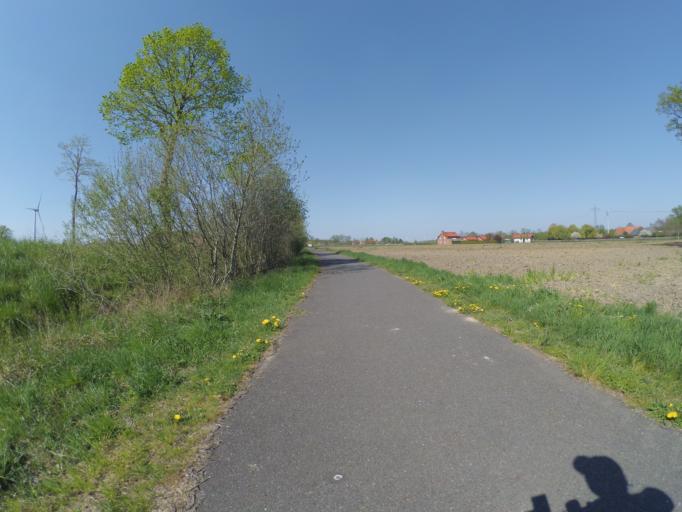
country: DE
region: North Rhine-Westphalia
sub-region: Regierungsbezirk Munster
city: Ascheberg
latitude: 51.8641
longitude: 7.5944
